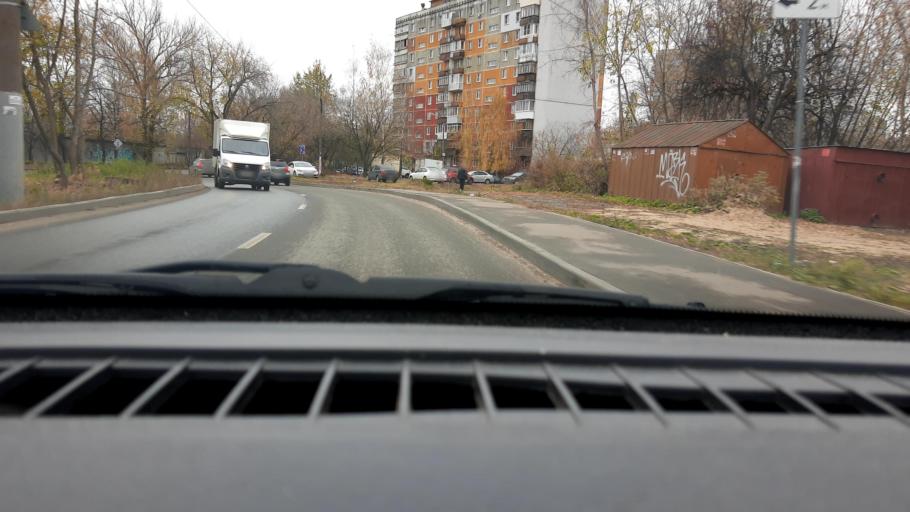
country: RU
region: Nizjnij Novgorod
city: Nizhniy Novgorod
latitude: 56.3327
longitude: 43.9261
